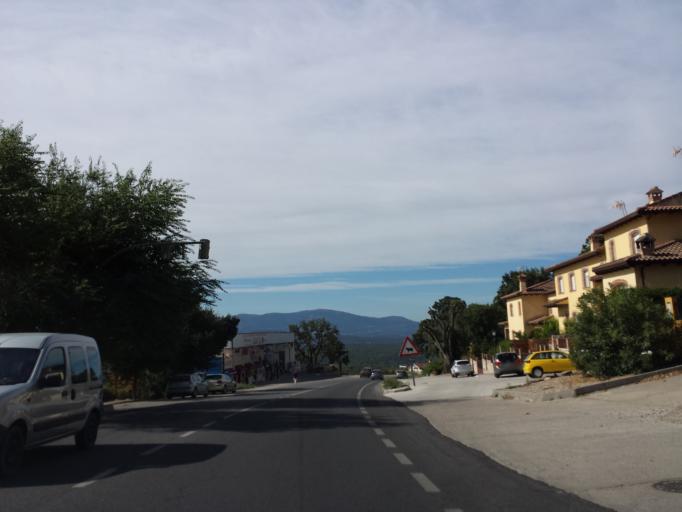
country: ES
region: Castille and Leon
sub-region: Provincia de Avila
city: Piedralaves
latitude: 40.3134
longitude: -4.7025
